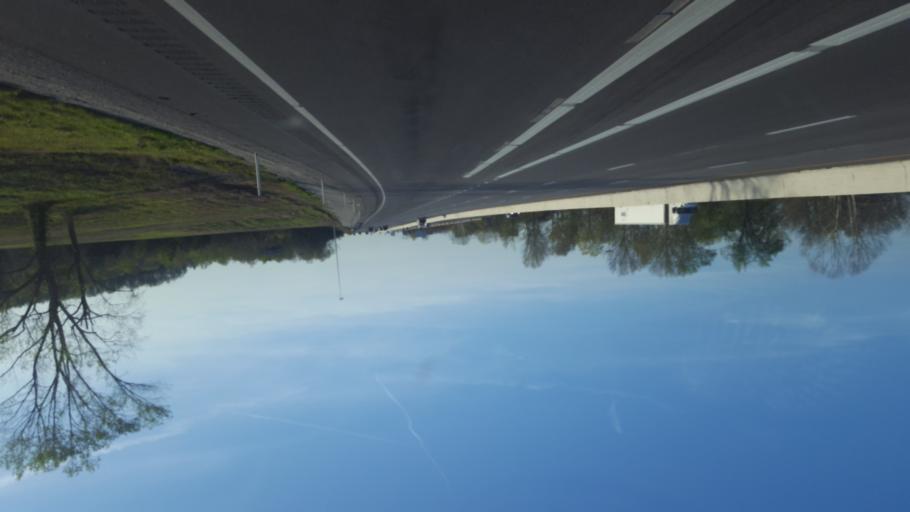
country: US
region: Kentucky
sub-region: Hart County
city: Munfordville
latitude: 37.2943
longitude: -85.9021
